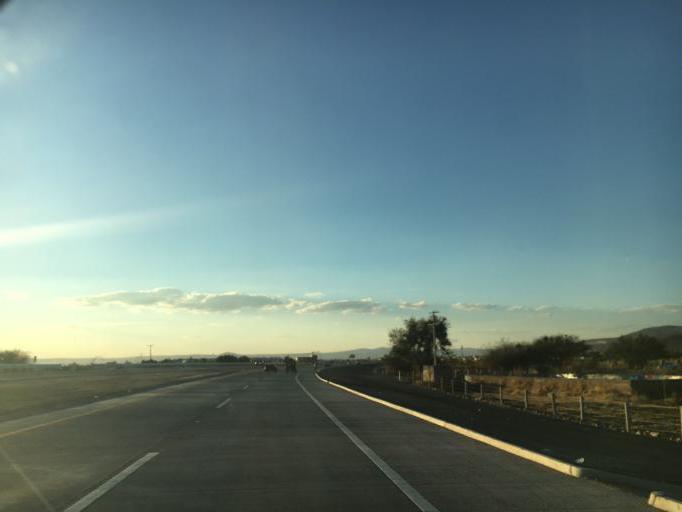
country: MX
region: Guanajuato
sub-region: Leon
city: Fraccionamiento Paraiso Real
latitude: 21.0980
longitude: -101.5703
